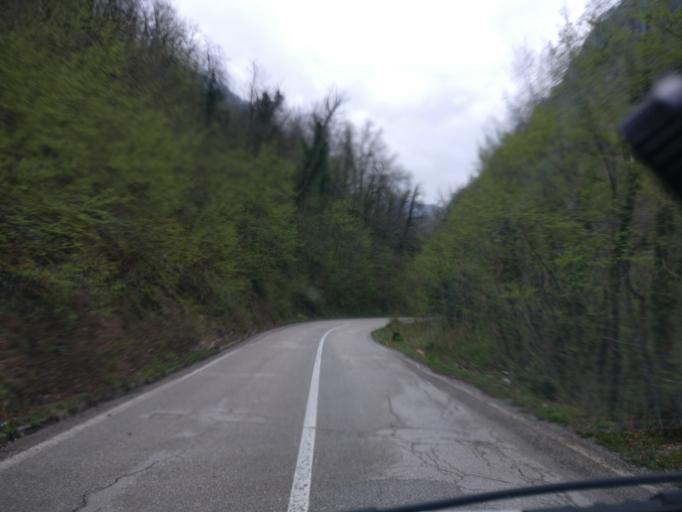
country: ME
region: Opstina Pluzine
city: Pluzine
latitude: 43.3046
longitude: 18.8503
